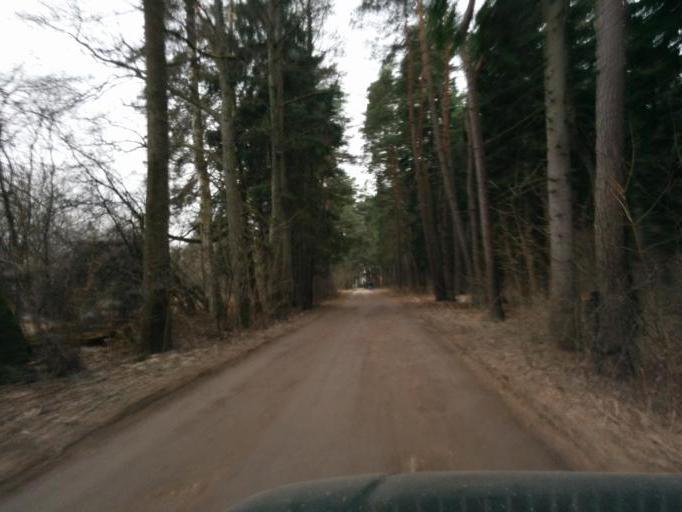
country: LV
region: Jurmala
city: Jurmala
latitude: 56.9686
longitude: 23.8407
